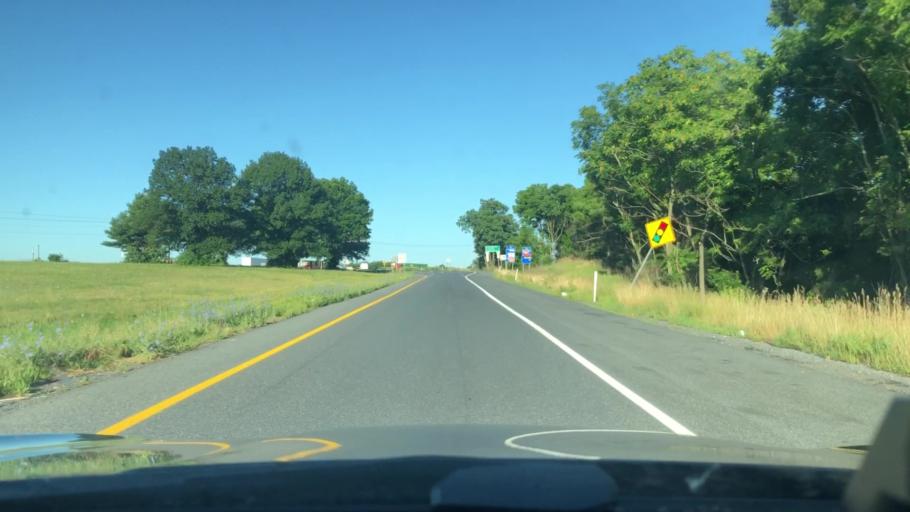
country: US
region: Pennsylvania
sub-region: Dauphin County
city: Skyline View
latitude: 40.3543
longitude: -76.7202
